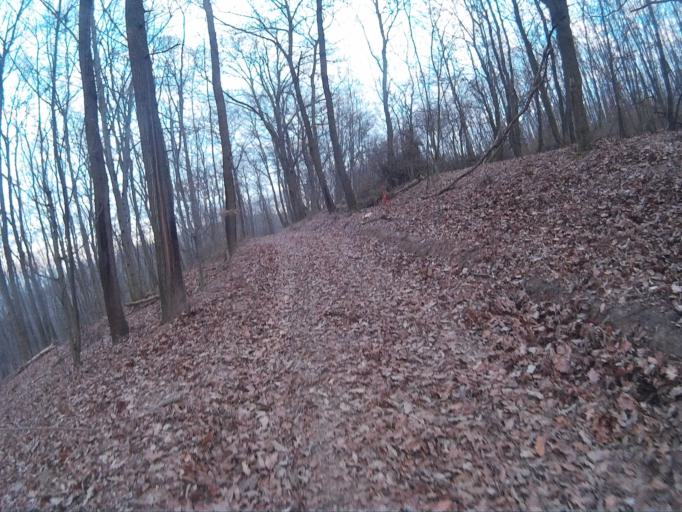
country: HU
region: Nograd
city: Rimoc
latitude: 48.0032
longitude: 19.4395
